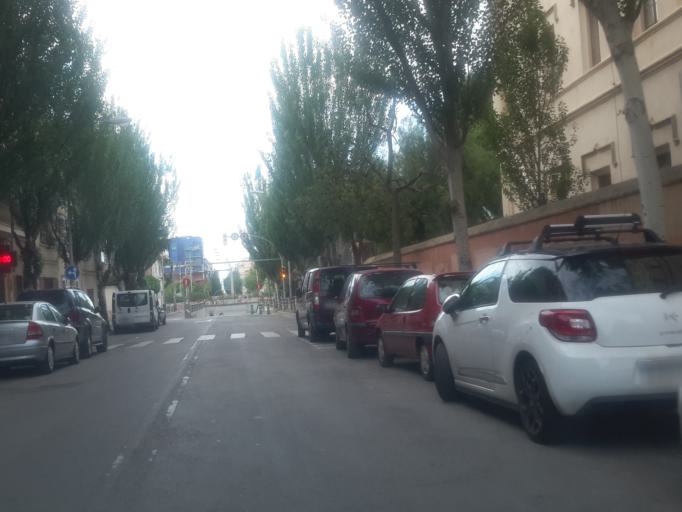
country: ES
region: Catalonia
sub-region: Provincia de Barcelona
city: Vilanova i la Geltru
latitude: 41.2196
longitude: 1.7247
